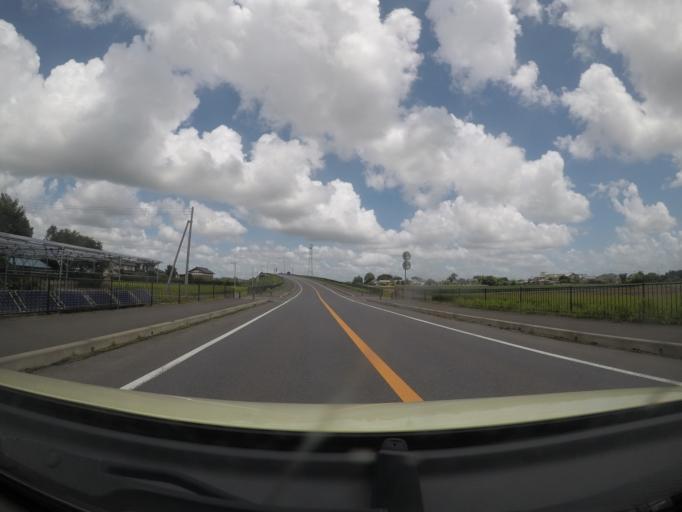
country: JP
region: Ibaraki
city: Mitsukaido
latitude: 36.0646
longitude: 139.9829
